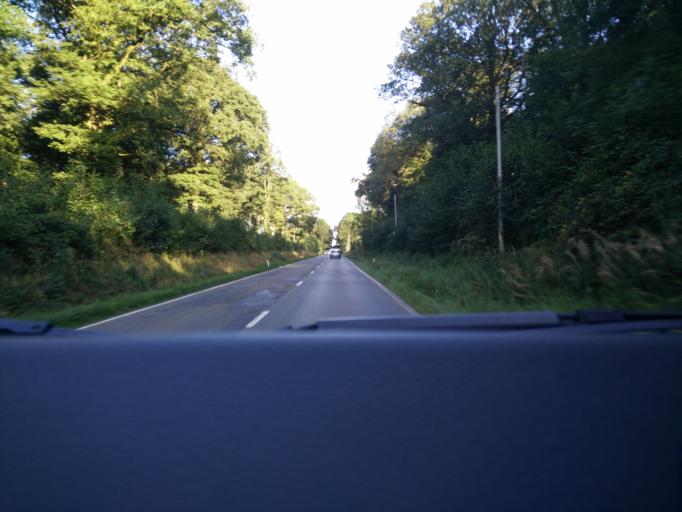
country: BE
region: Wallonia
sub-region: Province de Namur
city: Philippeville
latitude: 50.2043
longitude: 4.4846
